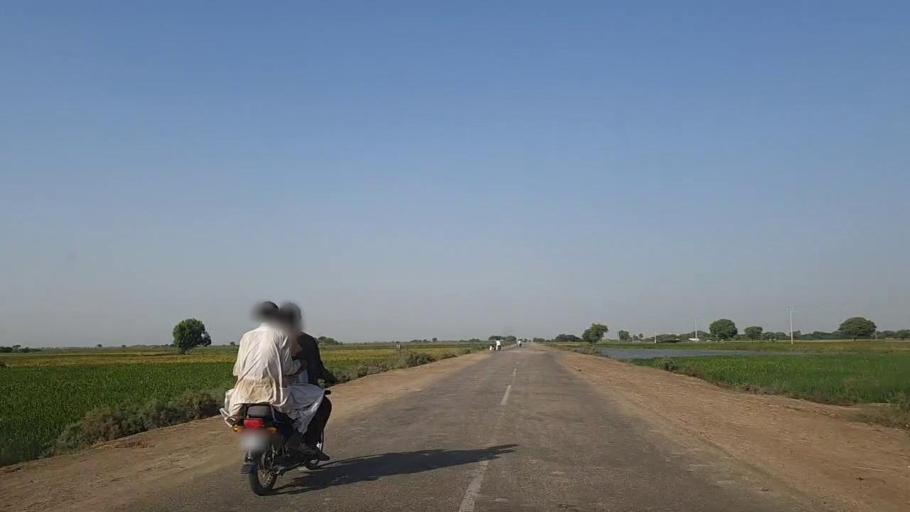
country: PK
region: Sindh
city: Mirpur Batoro
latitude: 24.5883
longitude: 68.3976
